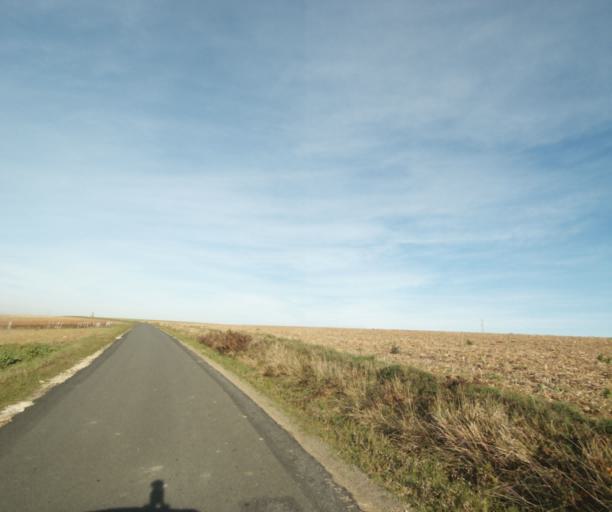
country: FR
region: Poitou-Charentes
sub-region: Departement de la Charente-Maritime
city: Chaniers
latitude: 45.7162
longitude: -0.5294
